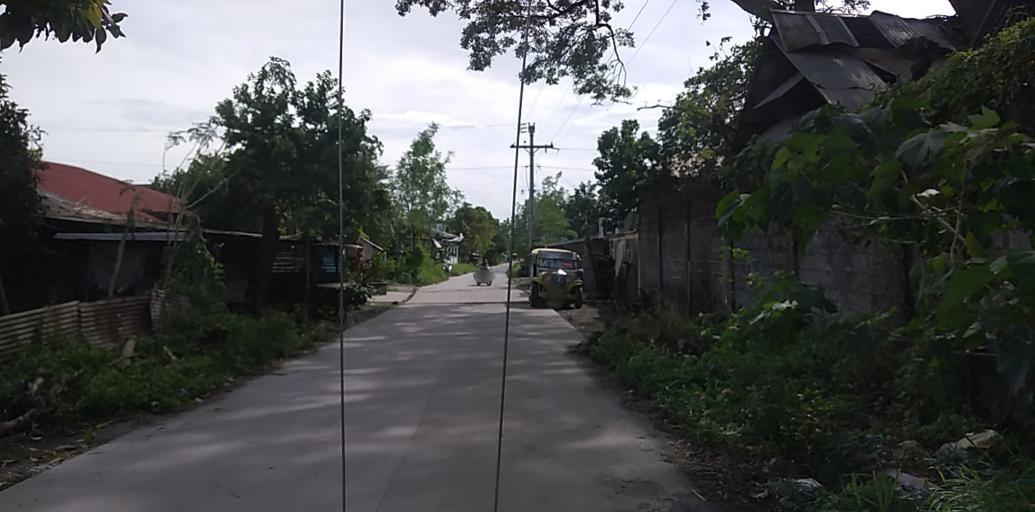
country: PH
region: Central Luzon
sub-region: Province of Pampanga
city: Angeles City
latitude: 15.1292
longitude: 120.5617
